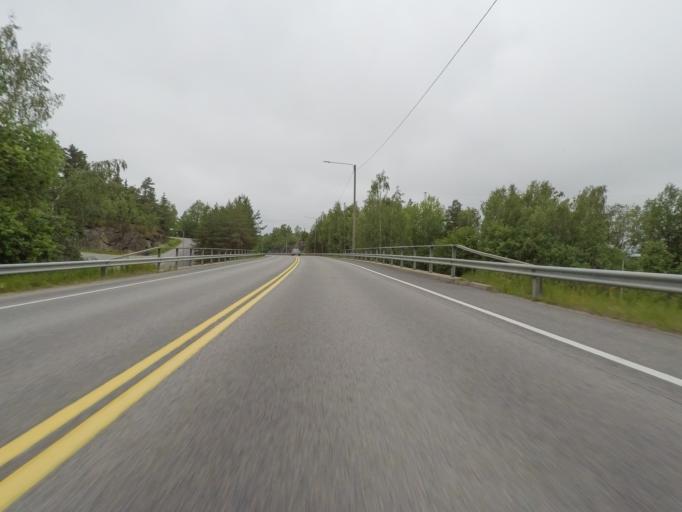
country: FI
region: Varsinais-Suomi
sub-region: Turku
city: Raisio
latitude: 60.4670
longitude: 22.1294
